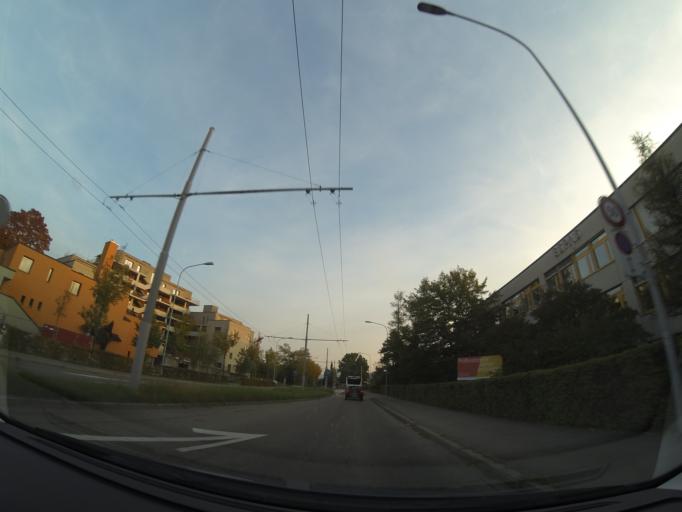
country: CH
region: Zurich
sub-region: Bezirk Zuerich
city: Zuerich (Kreis 10) / Ruetihof
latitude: 47.4138
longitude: 8.4835
